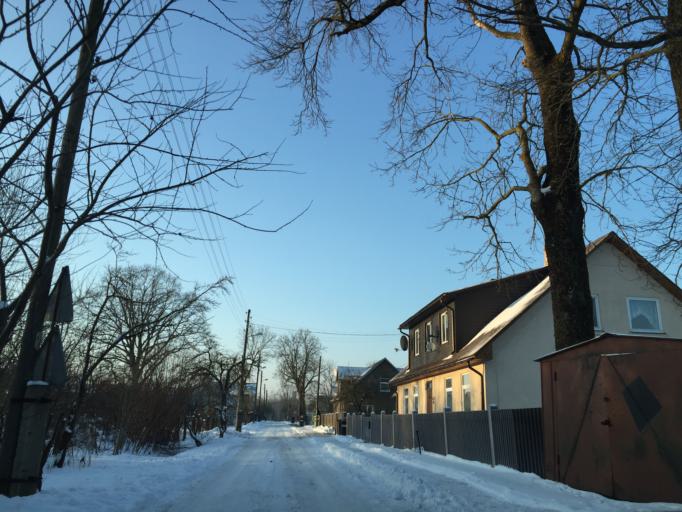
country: LV
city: Tireli
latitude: 56.9409
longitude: 23.6129
